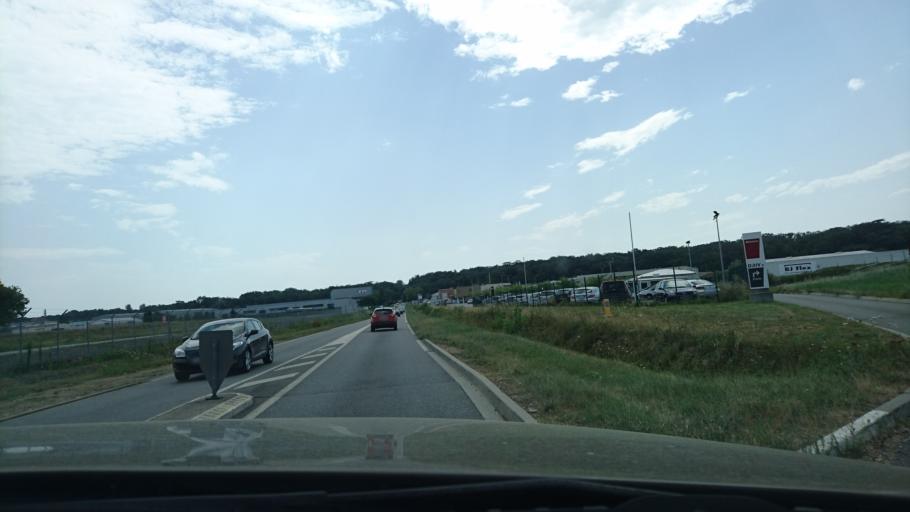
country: FR
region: Midi-Pyrenees
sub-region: Departement de la Haute-Garonne
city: Cornebarrieu
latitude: 43.6505
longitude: 1.3393
